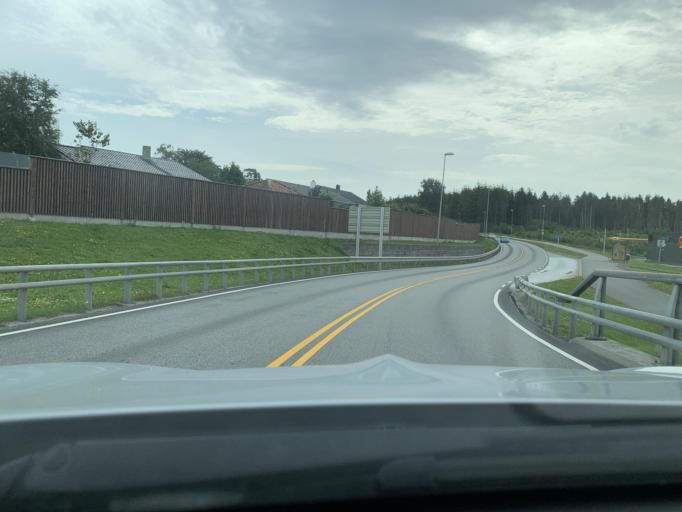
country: NO
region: Rogaland
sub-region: Sandnes
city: Sandnes
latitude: 58.7863
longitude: 5.7058
